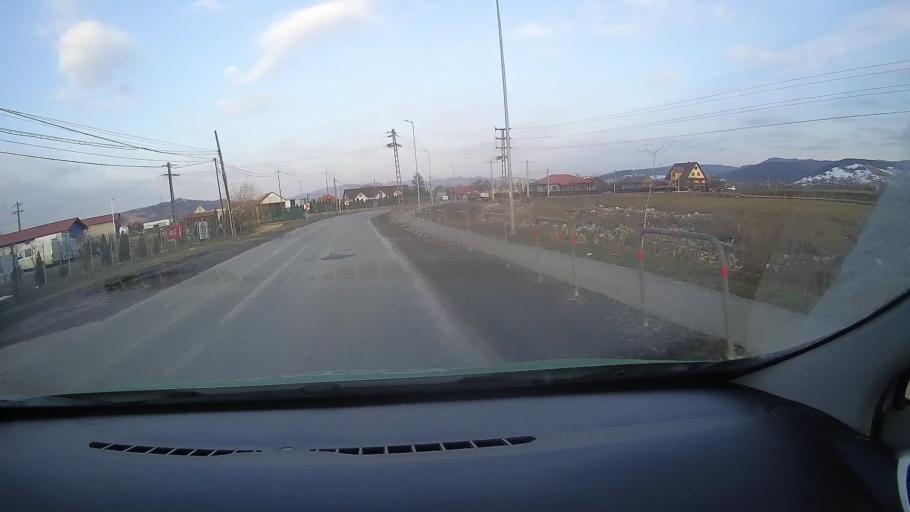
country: RO
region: Harghita
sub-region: Oras Cristuru Secuiesc
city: Filias
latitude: 46.2825
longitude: 25.0161
